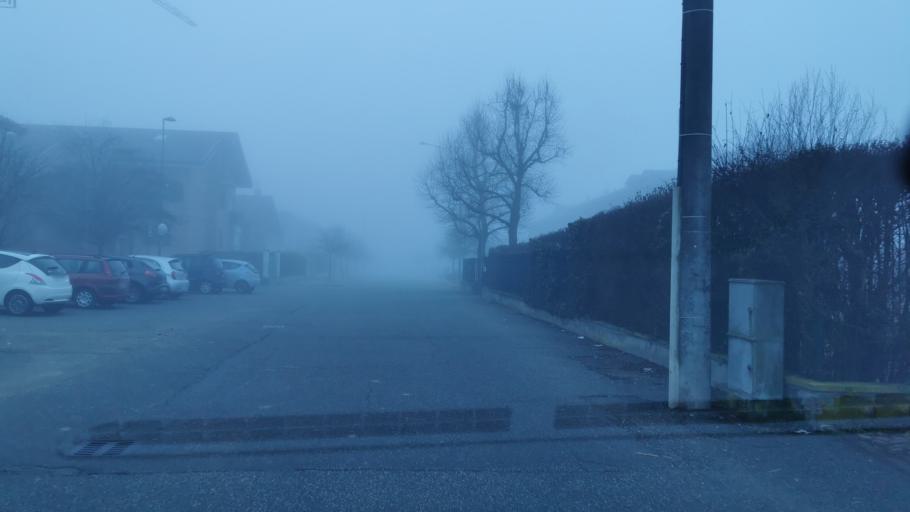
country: IT
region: Piedmont
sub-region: Provincia di Torino
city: Volpiano
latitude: 45.1936
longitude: 7.7663
